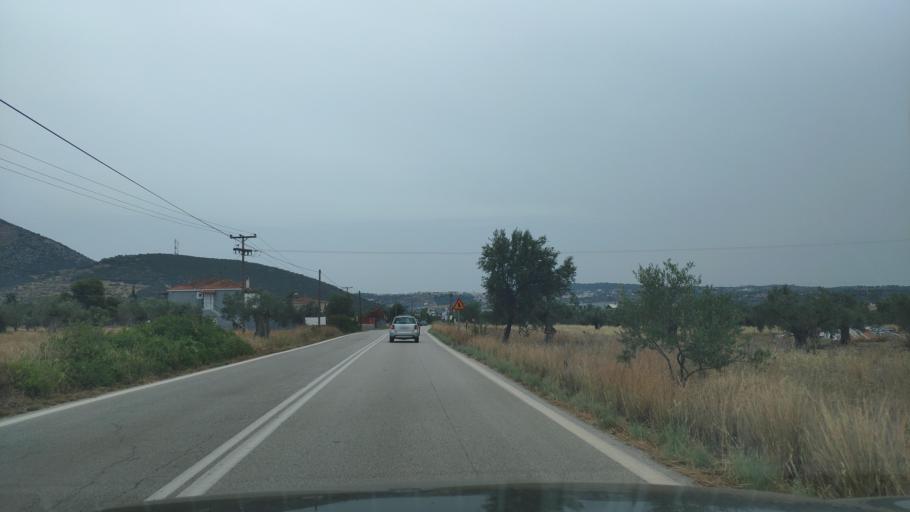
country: GR
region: Peloponnese
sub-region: Nomos Argolidos
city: Koilas
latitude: 37.4086
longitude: 23.1538
